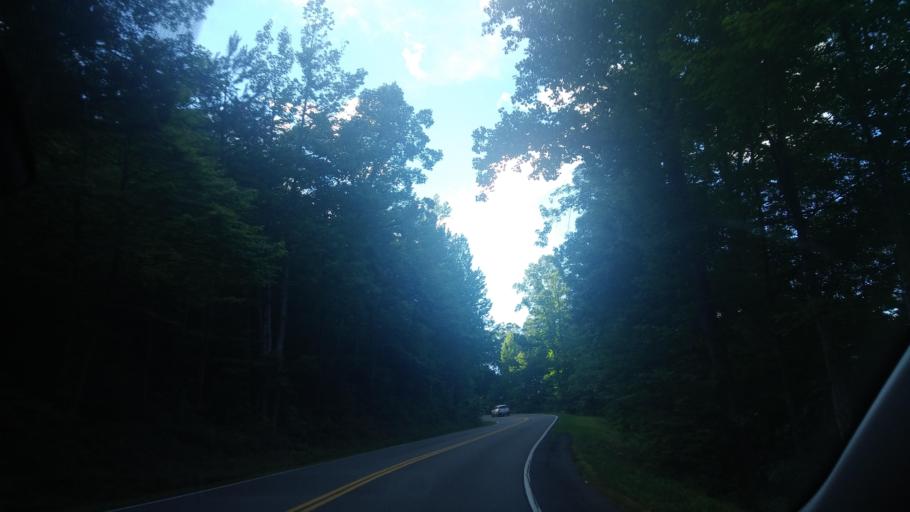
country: US
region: Tennessee
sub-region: Cocke County
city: Newport
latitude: 35.8048
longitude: -83.2406
